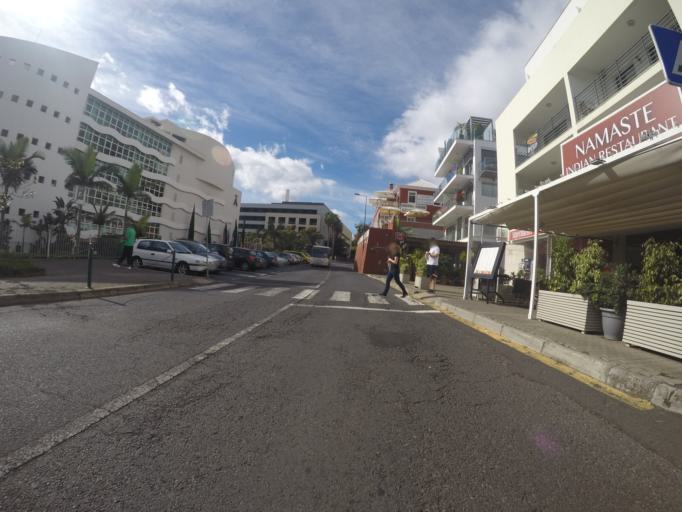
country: PT
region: Madeira
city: Camara de Lobos
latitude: 32.6382
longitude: -16.9341
